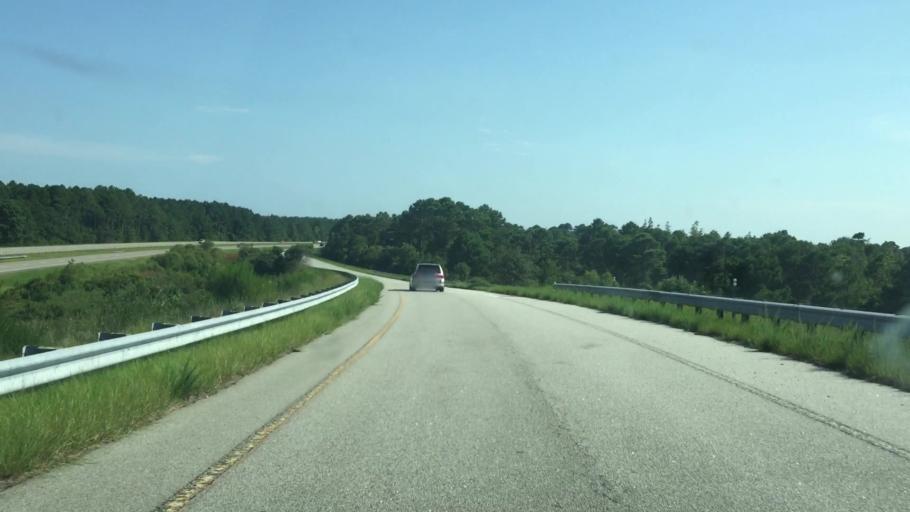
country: US
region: South Carolina
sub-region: Horry County
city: North Myrtle Beach
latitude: 33.8084
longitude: -78.7800
